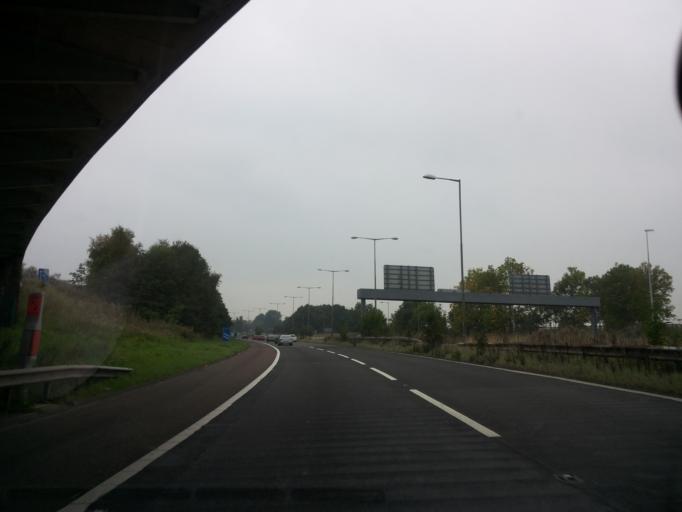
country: GB
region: England
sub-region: Lancashire
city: Goosnargh
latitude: 53.8063
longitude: -2.7009
